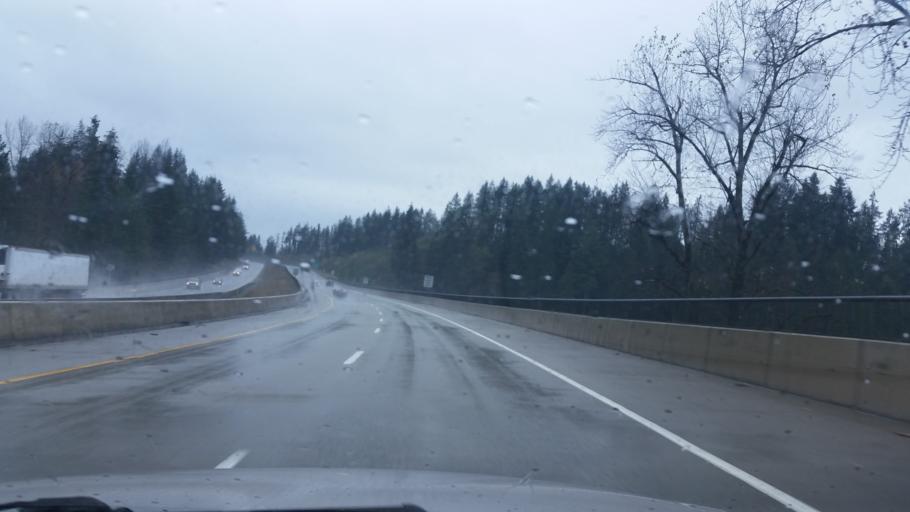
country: US
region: Washington
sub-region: King County
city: Maple Valley
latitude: 47.4069
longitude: -122.0414
